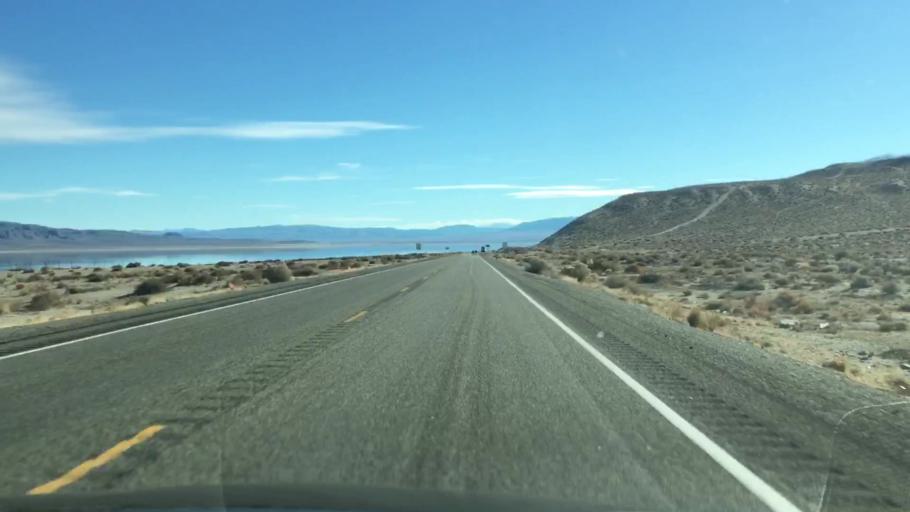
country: US
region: Nevada
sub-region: Mineral County
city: Hawthorne
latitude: 38.7878
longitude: -118.7539
